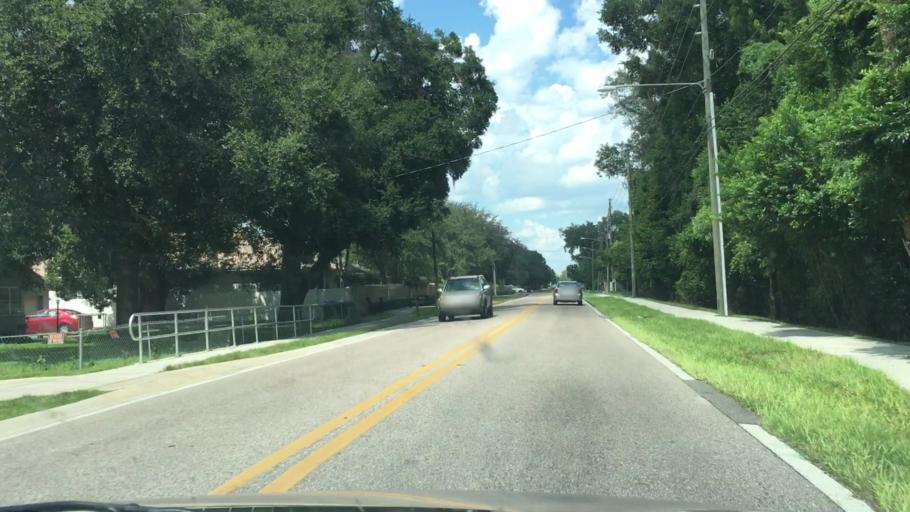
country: US
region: Florida
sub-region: Orange County
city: Lockhart
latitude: 28.6315
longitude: -81.4436
